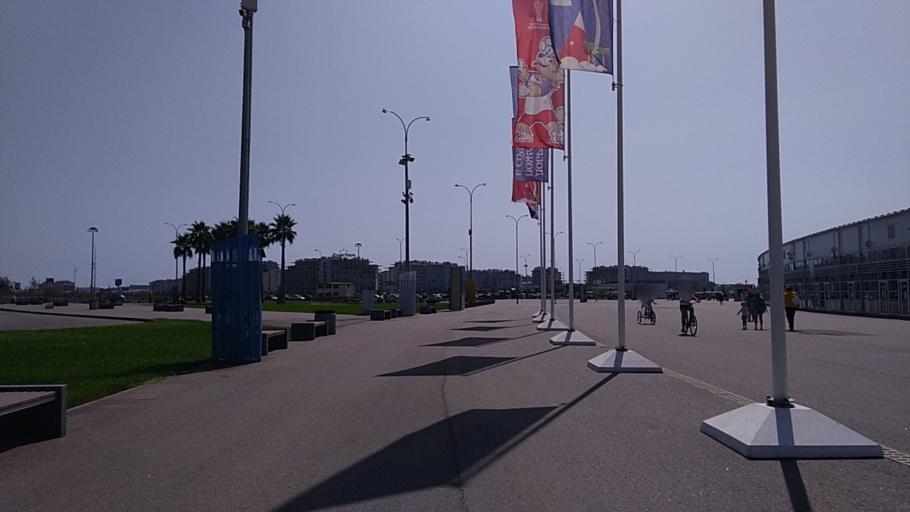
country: RU
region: Krasnodarskiy
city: Adler
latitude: 43.4093
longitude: 39.9726
